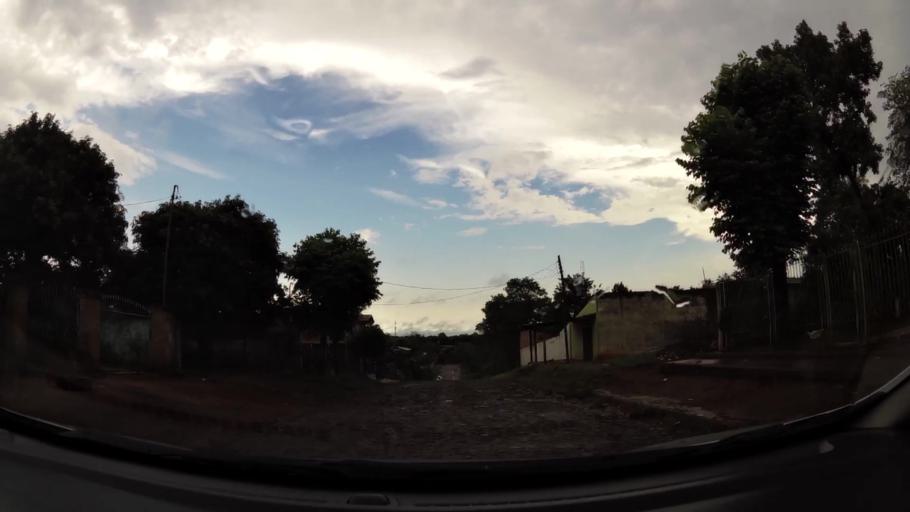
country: PY
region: Alto Parana
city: Presidente Franco
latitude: -25.5411
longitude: -54.6525
